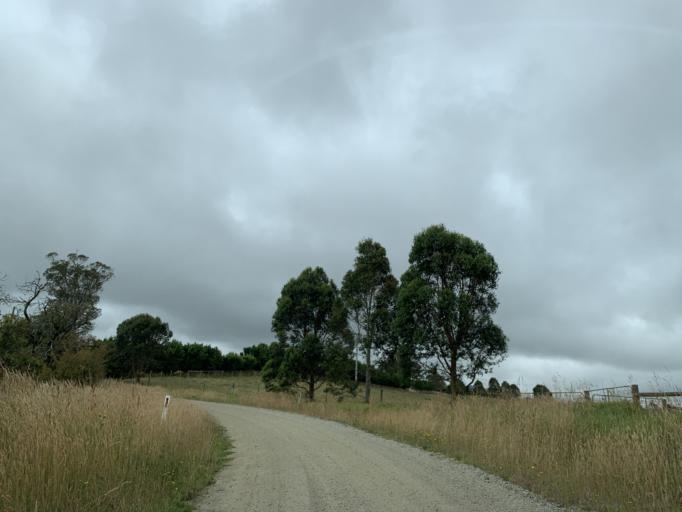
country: AU
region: Victoria
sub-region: Baw Baw
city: Warragul
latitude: -38.2877
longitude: 145.8773
